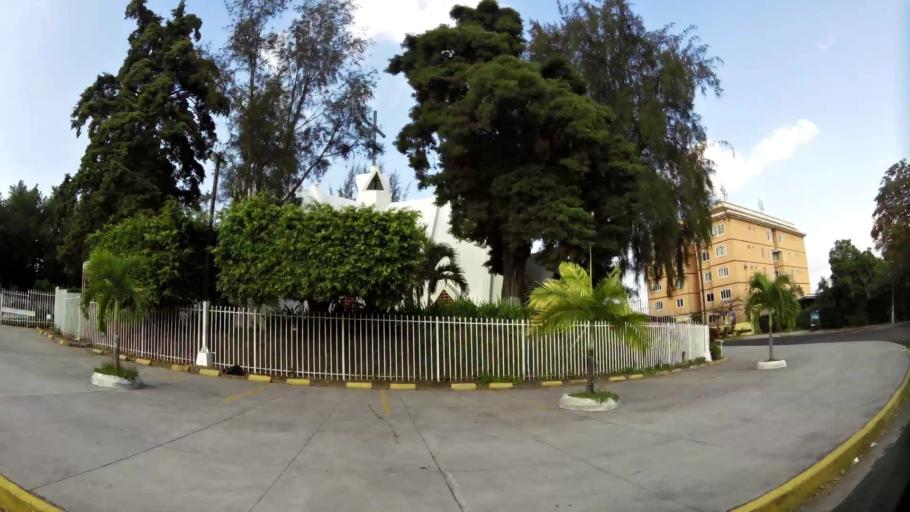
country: SV
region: La Libertad
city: Antiguo Cuscatlan
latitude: 13.6935
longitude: -89.2395
